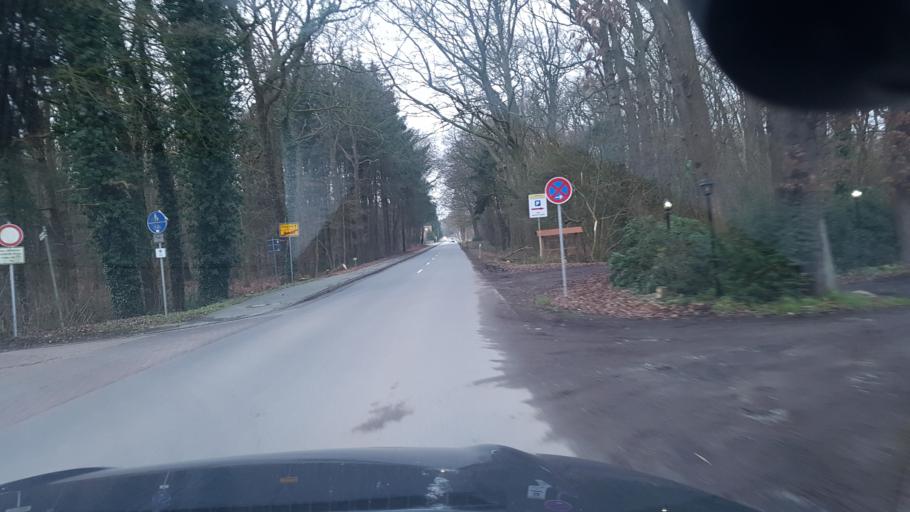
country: DE
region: Lower Saxony
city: Langen
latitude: 53.6074
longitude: 8.6678
